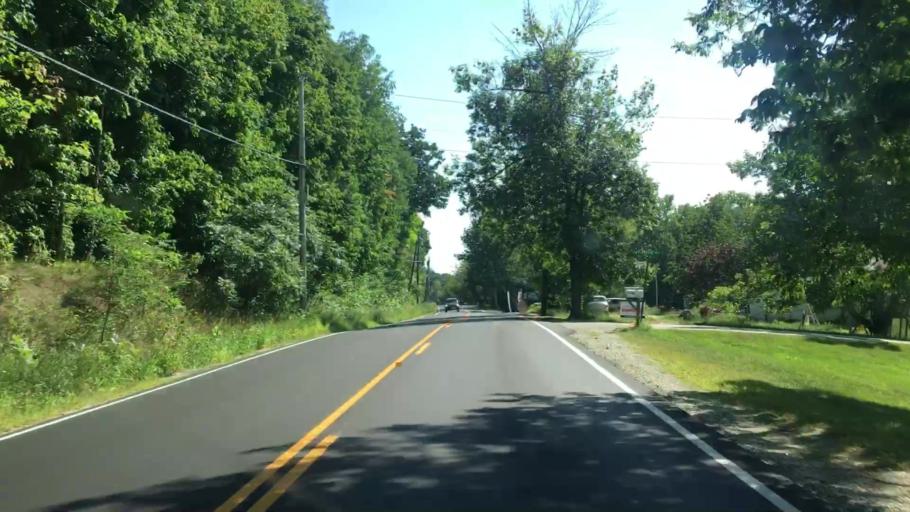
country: US
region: Maine
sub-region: Androscoggin County
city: Sabattus
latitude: 44.1351
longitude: -70.0873
